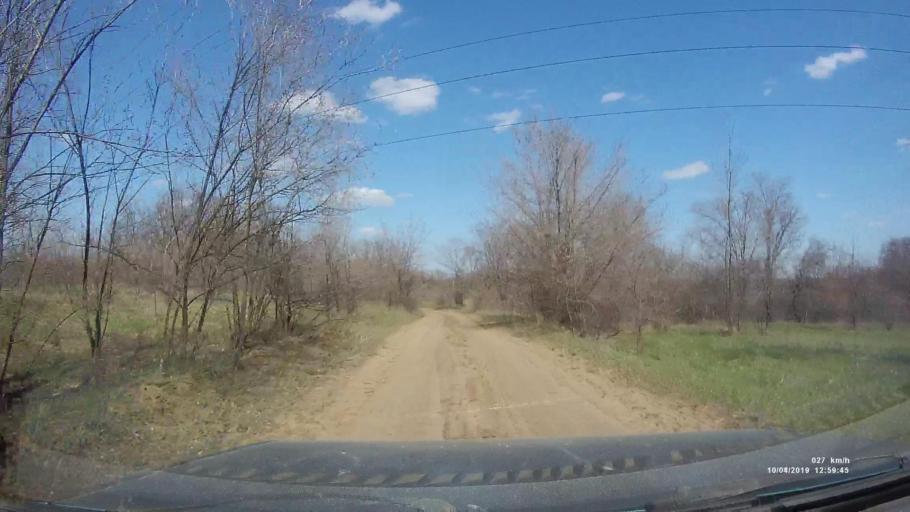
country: RU
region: Rostov
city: Masalovka
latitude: 48.3786
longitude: 40.2288
